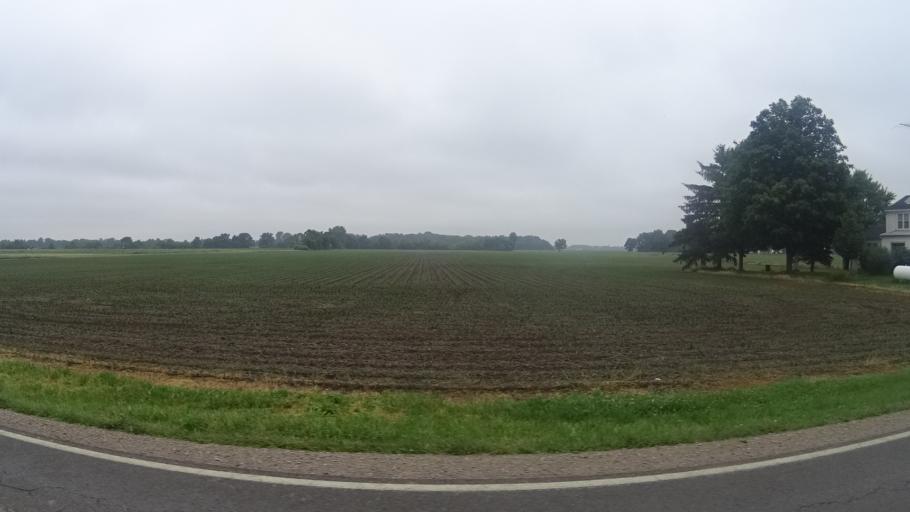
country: US
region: Ohio
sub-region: Erie County
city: Milan
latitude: 41.3588
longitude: -82.6219
